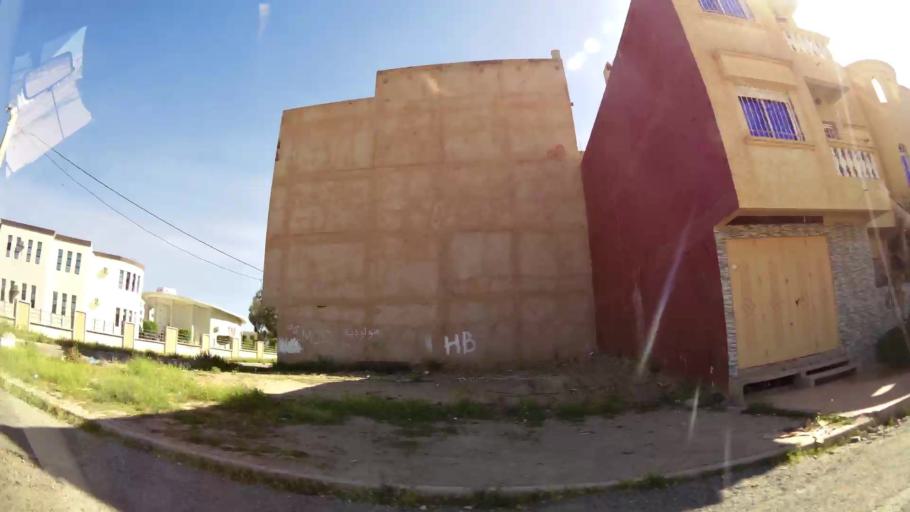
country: MA
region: Oriental
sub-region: Oujda-Angad
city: Oujda
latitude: 34.6618
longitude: -1.9129
